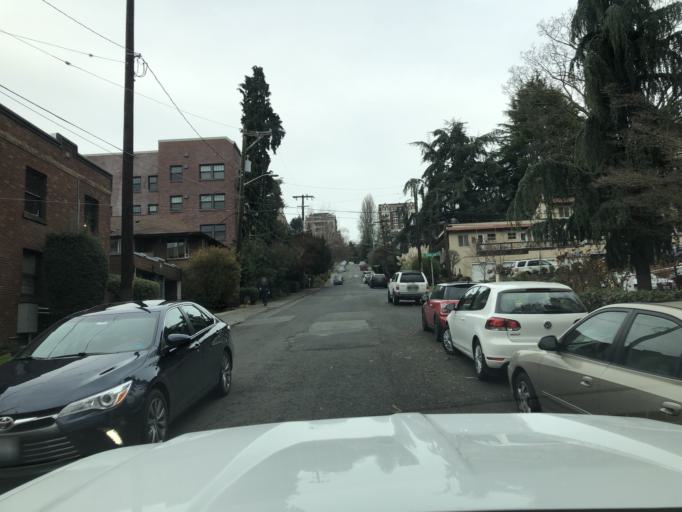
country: US
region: Washington
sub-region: King County
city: Seattle
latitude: 47.6267
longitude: -122.3580
